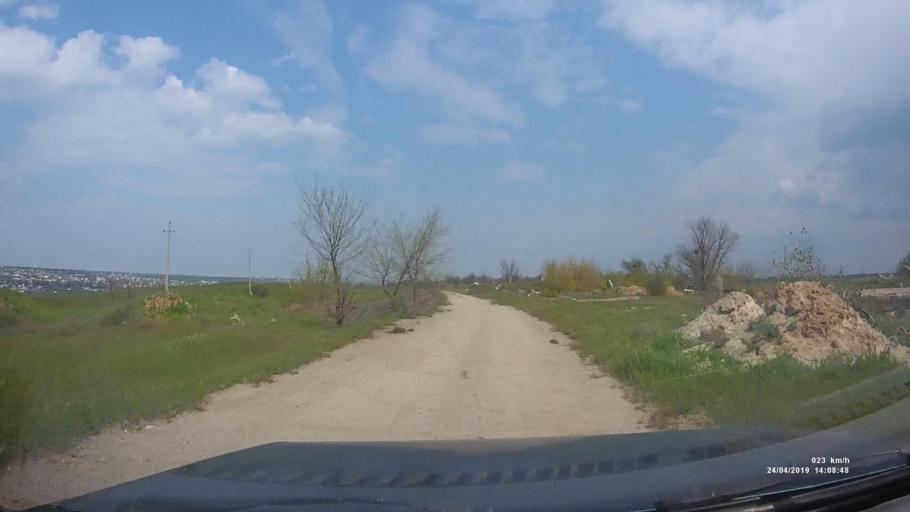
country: RU
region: Kalmykiya
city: Arshan'
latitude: 46.2636
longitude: 44.2195
